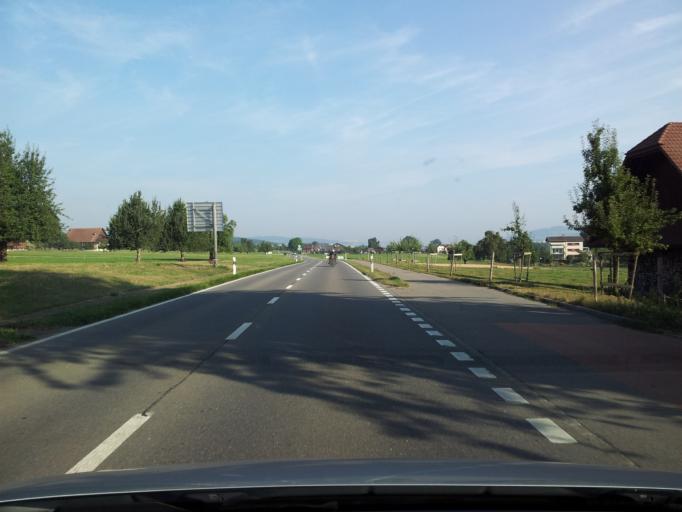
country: CH
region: Lucerne
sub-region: Sursee District
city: Nottwil
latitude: 47.1417
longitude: 8.1263
